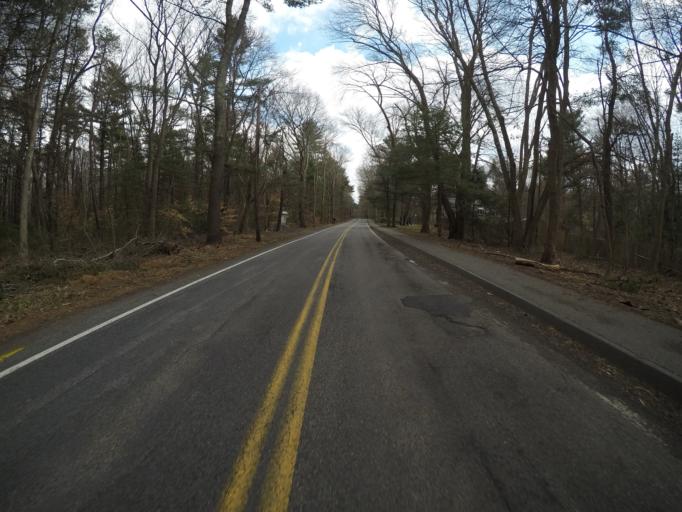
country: US
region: Massachusetts
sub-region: Bristol County
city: Easton
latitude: 42.0560
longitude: -71.1248
